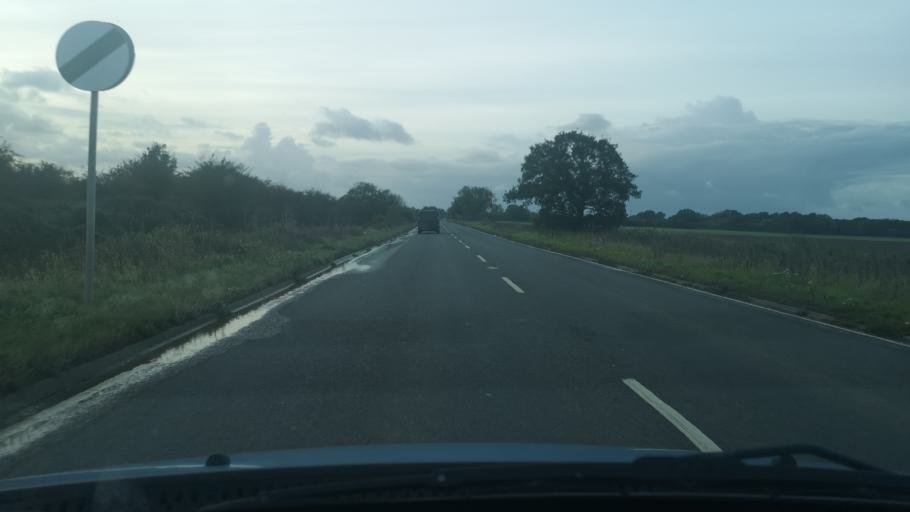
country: GB
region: England
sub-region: North Lincolnshire
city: Belton
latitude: 53.5816
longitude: -0.7971
